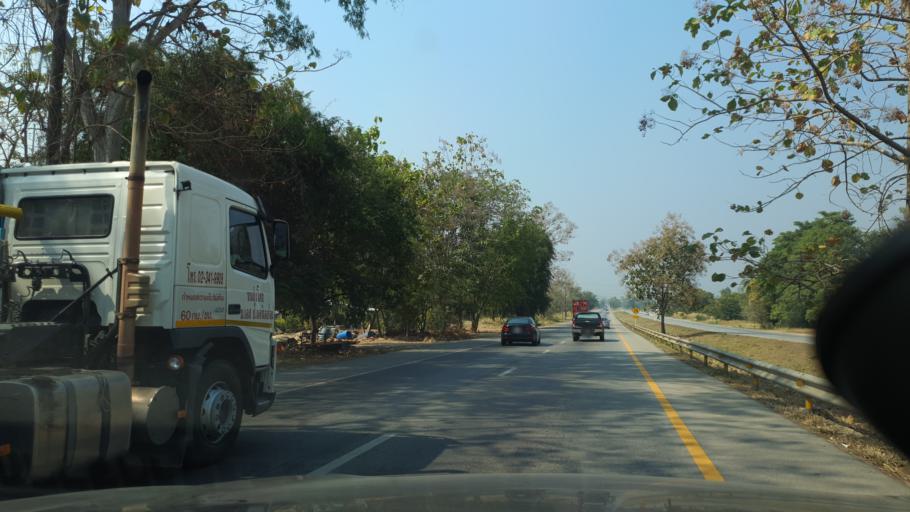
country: TH
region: Kamphaeng Phet
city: Kosamphi Nakhon
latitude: 16.6237
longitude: 99.3567
